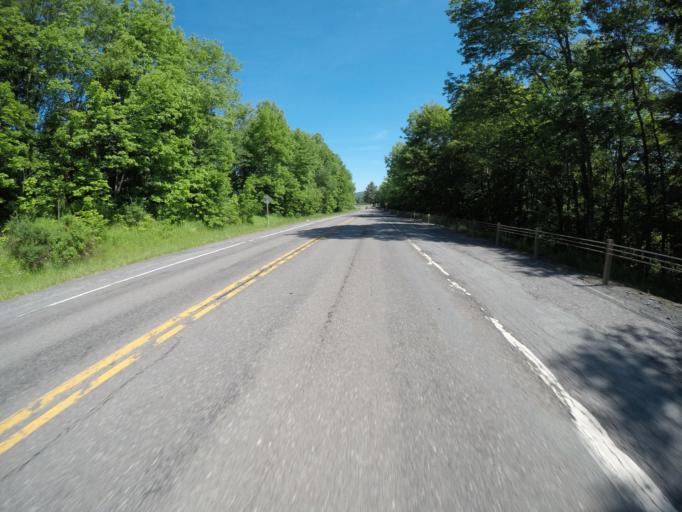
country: US
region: New York
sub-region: Delaware County
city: Delhi
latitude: 42.2180
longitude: -74.9675
